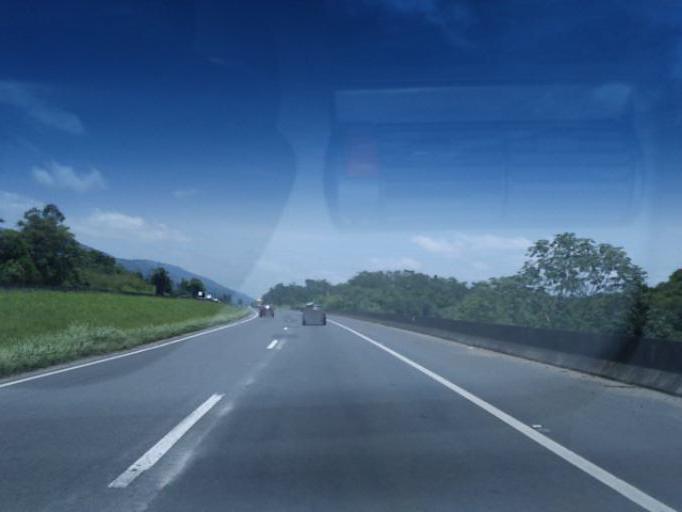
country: BR
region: Sao Paulo
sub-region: Miracatu
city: Miracatu
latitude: -24.2653
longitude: -47.3885
